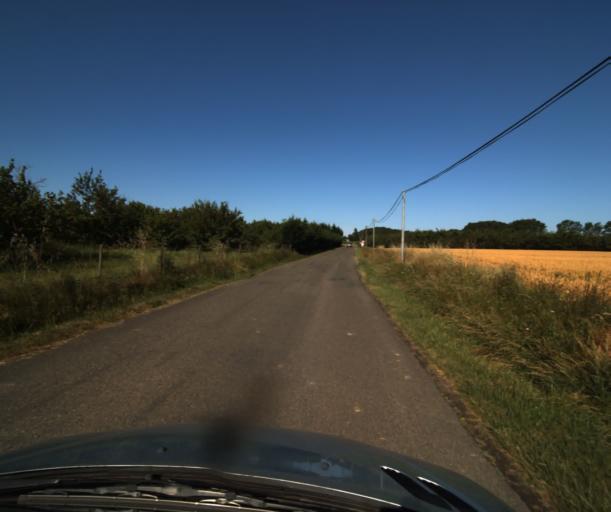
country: FR
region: Midi-Pyrenees
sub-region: Departement du Tarn-et-Garonne
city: Bressols
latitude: 43.9645
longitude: 1.3190
